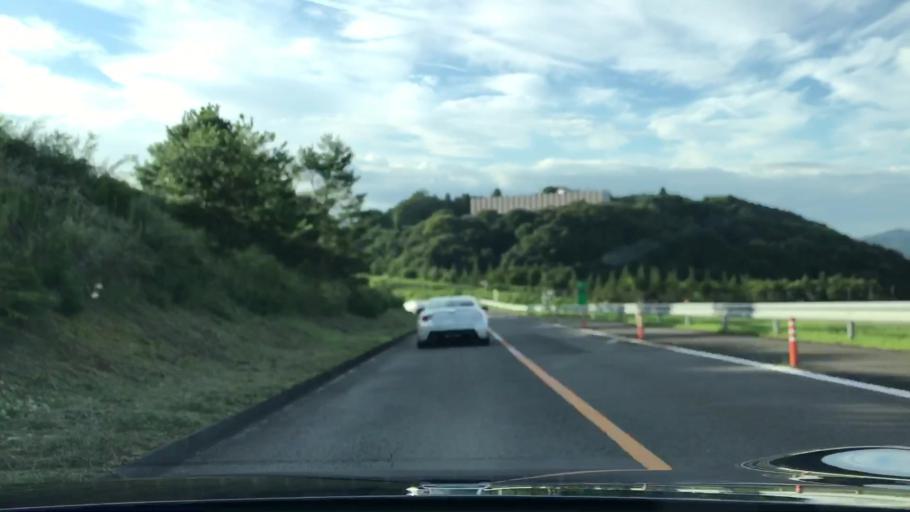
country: JP
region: Tochigi
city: Motegi
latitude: 36.5349
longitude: 140.2307
